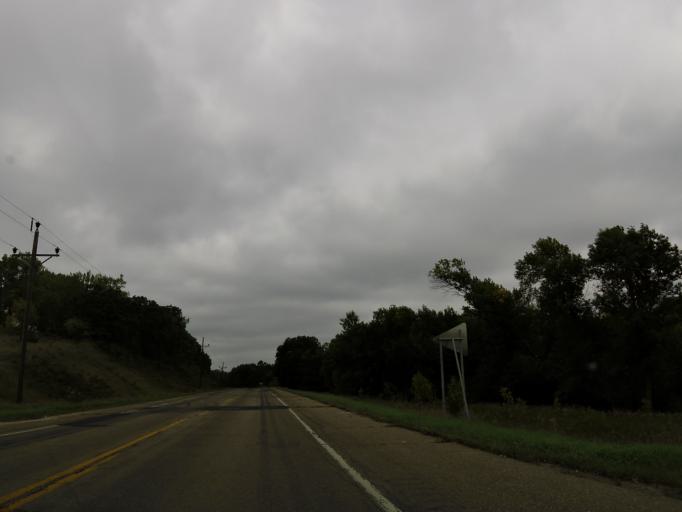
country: US
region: Minnesota
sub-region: Yellow Medicine County
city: Granite Falls
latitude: 44.8612
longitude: -95.6322
